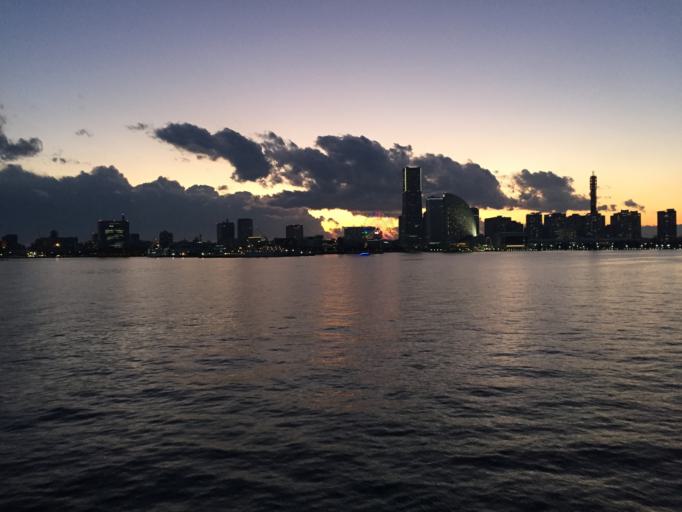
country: JP
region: Kanagawa
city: Yokohama
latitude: 35.4615
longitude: 139.6531
